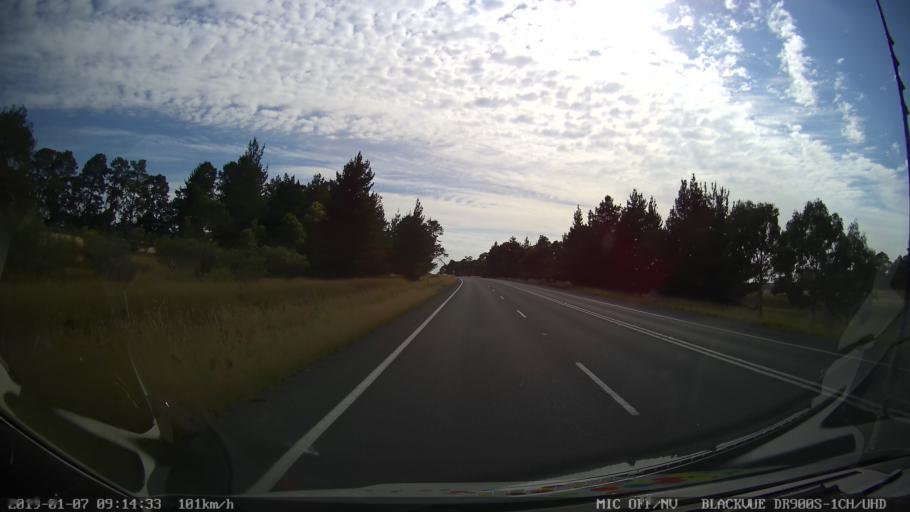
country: AU
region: New South Wales
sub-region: Armidale Dumaresq
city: Armidale
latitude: -30.6235
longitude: 151.5229
